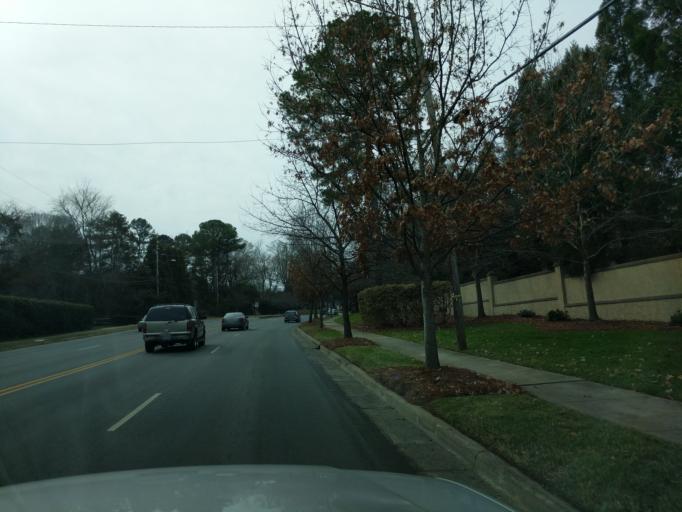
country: US
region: North Carolina
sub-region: Mecklenburg County
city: Charlotte
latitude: 35.1861
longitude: -80.8065
